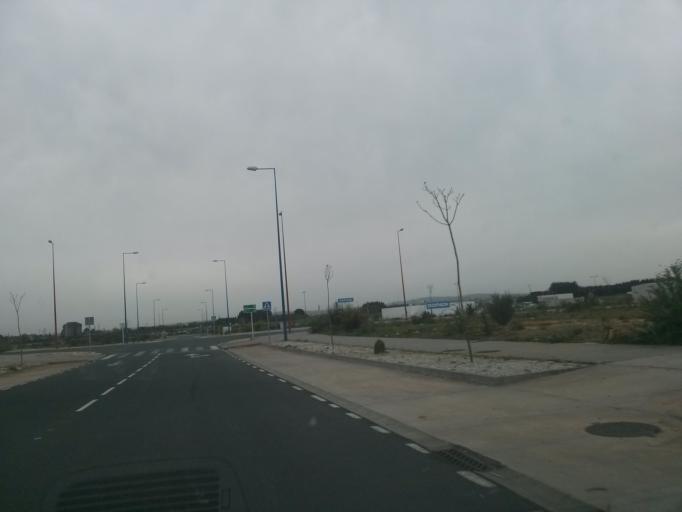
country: ES
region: Galicia
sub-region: Provincia de Lugo
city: Lugo
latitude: 43.0403
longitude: -7.5501
